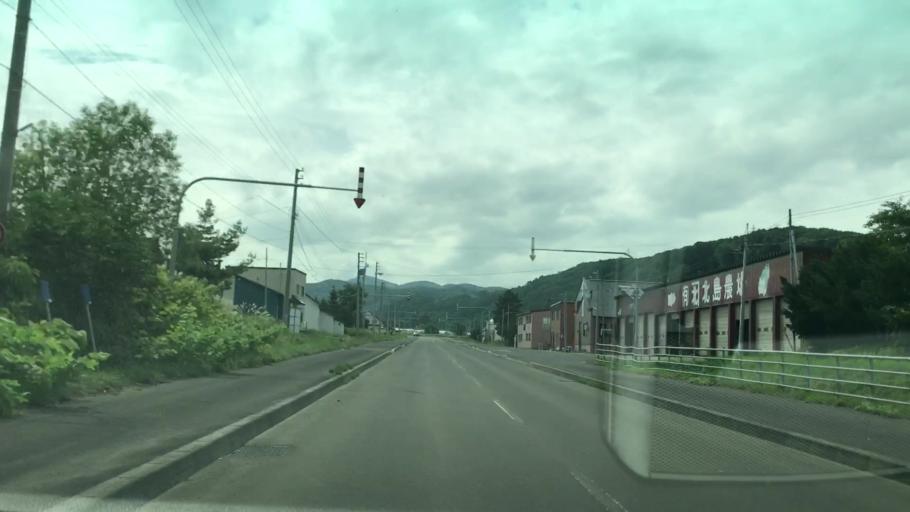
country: JP
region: Hokkaido
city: Yoichi
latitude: 43.1806
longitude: 140.8452
